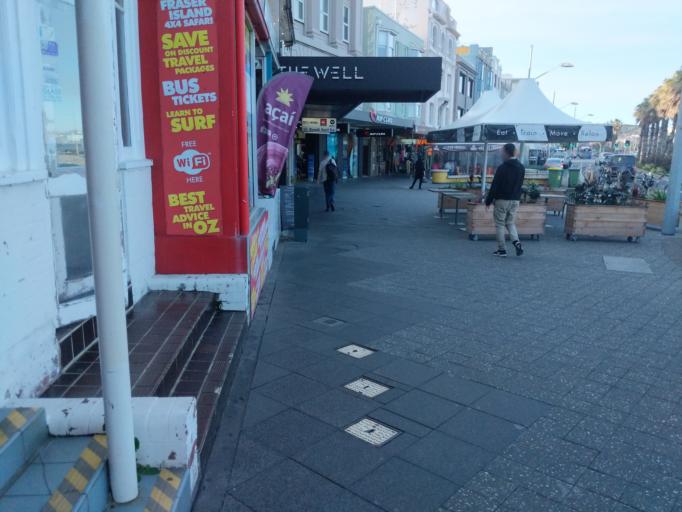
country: AU
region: New South Wales
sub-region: Waverley
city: Bondi Beach
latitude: -33.8922
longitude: 151.2729
